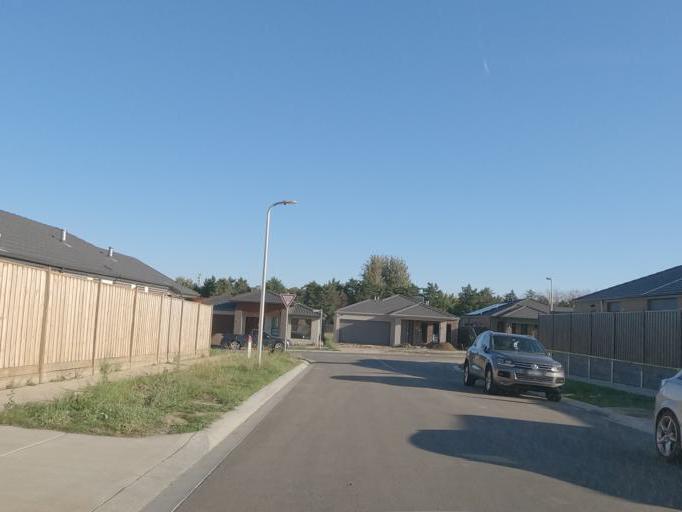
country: AU
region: Victoria
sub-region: Hume
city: Greenvale
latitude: -37.6425
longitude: 144.8735
